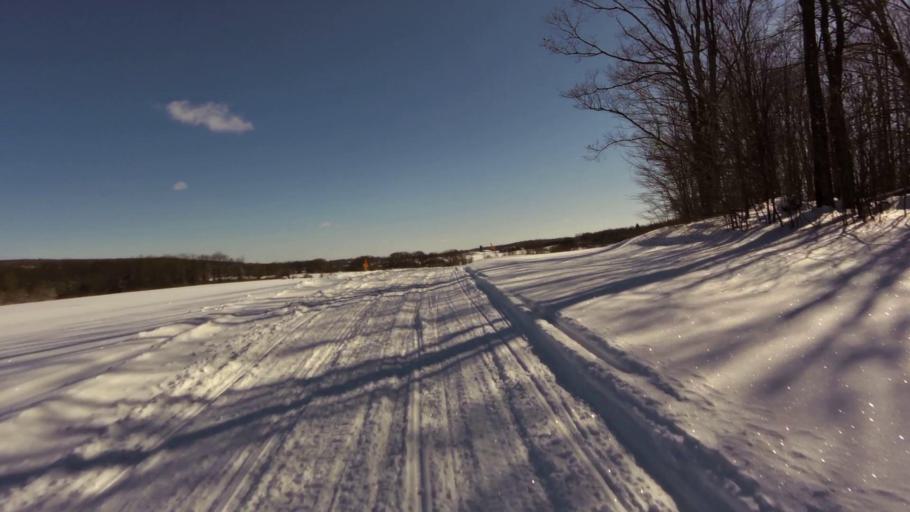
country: US
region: New York
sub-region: Chautauqua County
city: Fredonia
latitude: 42.3680
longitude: -79.1767
